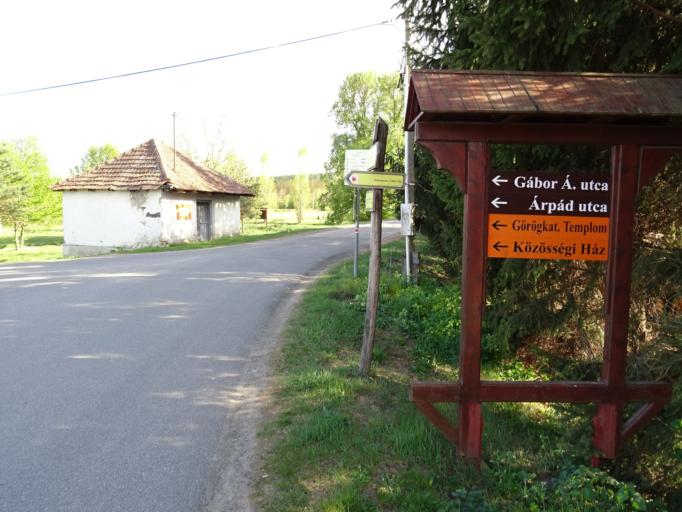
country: HU
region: Borsod-Abauj-Zemplen
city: Satoraljaujhely
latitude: 48.4641
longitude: 21.5912
